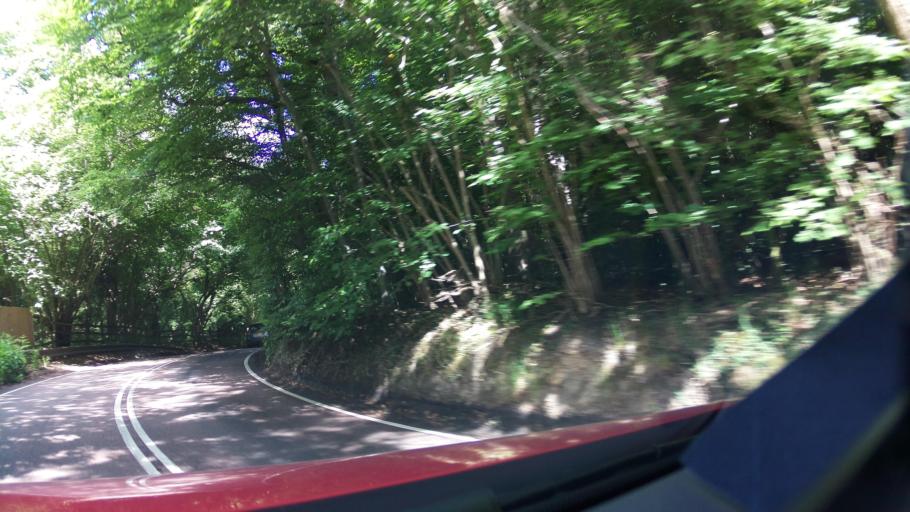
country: GB
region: England
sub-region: Hertfordshire
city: Kings Langley
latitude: 51.6752
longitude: -0.4508
